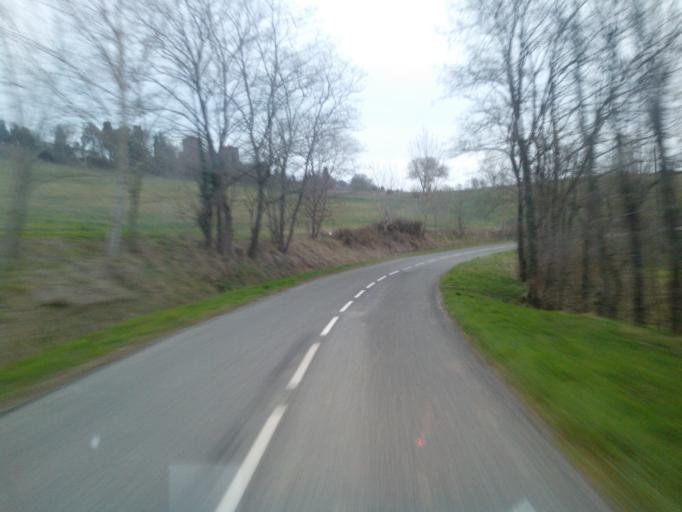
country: FR
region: Languedoc-Roussillon
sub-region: Departement de l'Aude
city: Belpech
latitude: 43.2632
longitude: 1.7482
